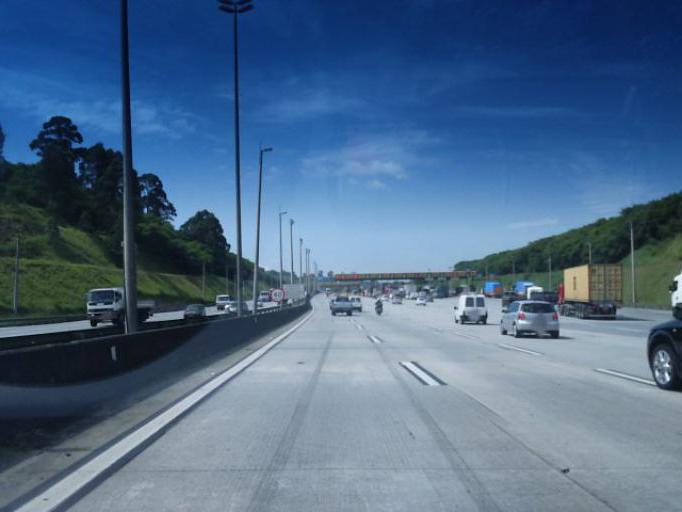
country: BR
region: Sao Paulo
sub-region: Taboao Da Serra
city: Taboao da Serra
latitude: -23.5982
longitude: -46.8120
